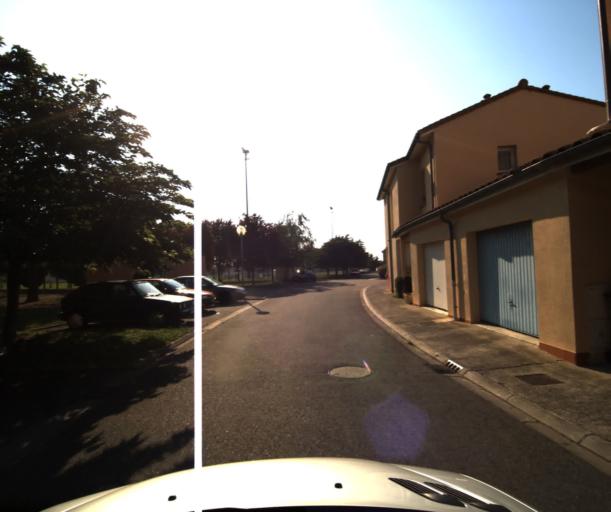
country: FR
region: Midi-Pyrenees
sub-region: Departement de la Haute-Garonne
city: Labarthe-sur-Leze
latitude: 43.4783
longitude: 1.3925
